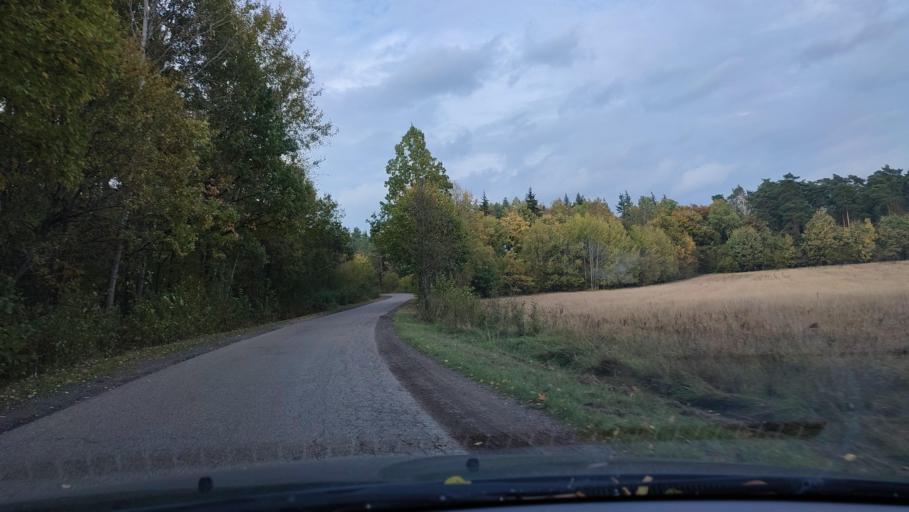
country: PL
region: Masovian Voivodeship
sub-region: Powiat mlawski
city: Mlawa
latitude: 53.1462
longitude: 20.3687
